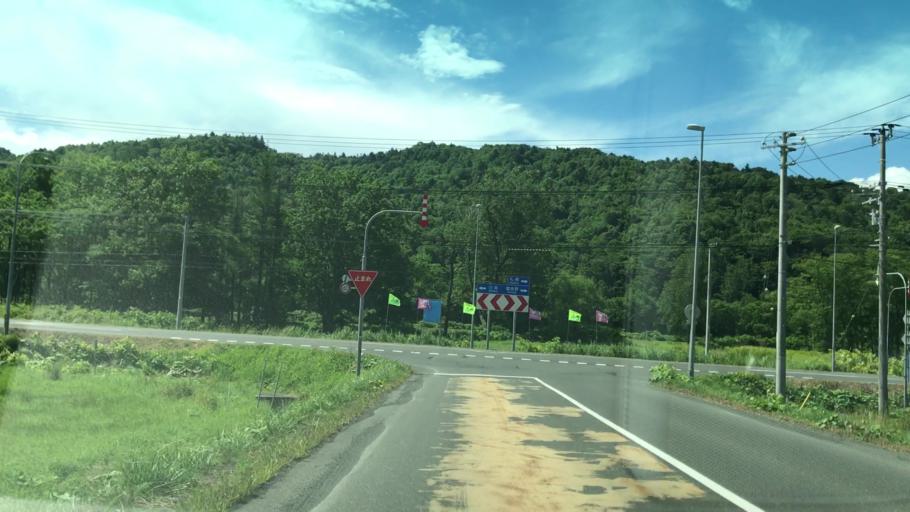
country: JP
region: Hokkaido
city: Shimo-furano
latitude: 42.9759
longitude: 142.4118
